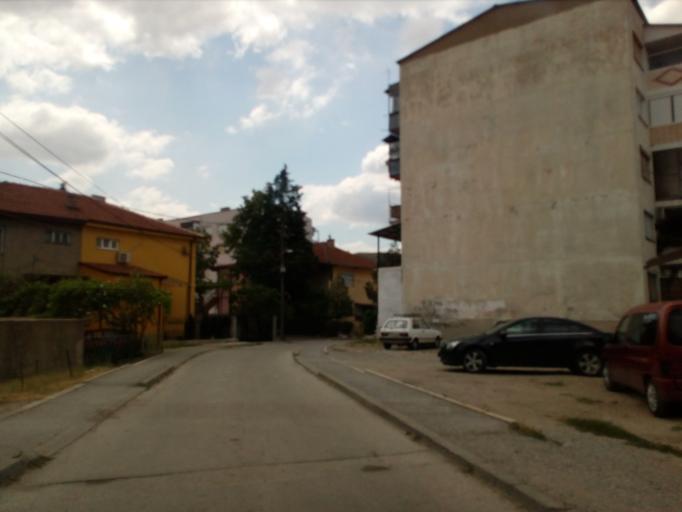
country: MK
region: Veles
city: Veles
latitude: 41.7180
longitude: 21.7647
